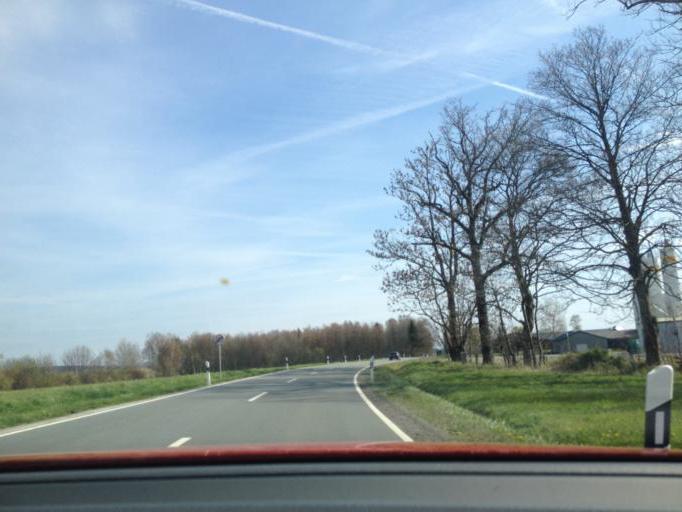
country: DE
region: Bavaria
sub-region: Upper Franconia
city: Munchberg
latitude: 50.1735
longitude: 11.7494
